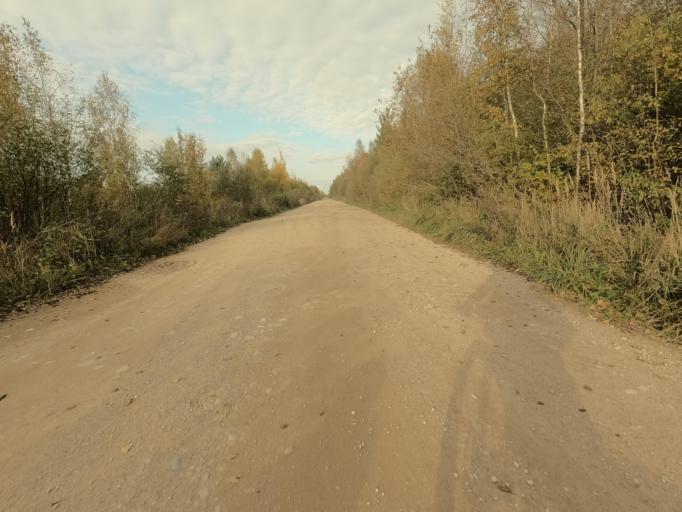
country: RU
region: Novgorod
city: Volkhovskiy
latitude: 58.9082
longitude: 31.0381
